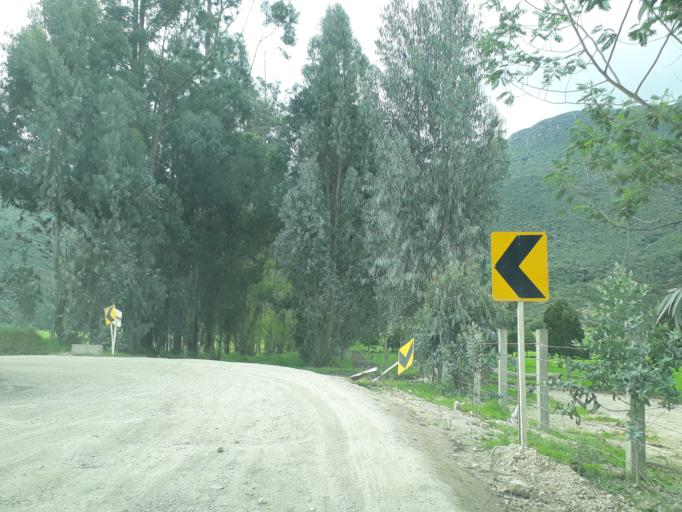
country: CO
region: Cundinamarca
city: Lenguazaque
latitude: 5.3220
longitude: -73.7455
